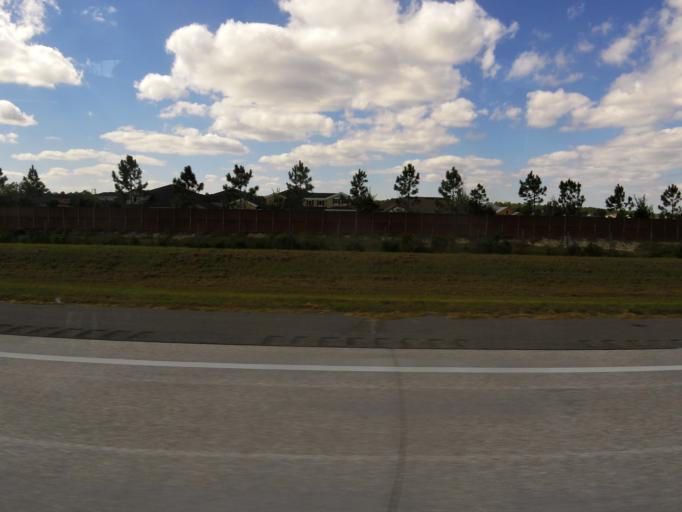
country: US
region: Florida
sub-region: Saint Johns County
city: Fruit Cove
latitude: 30.1074
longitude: -81.5158
